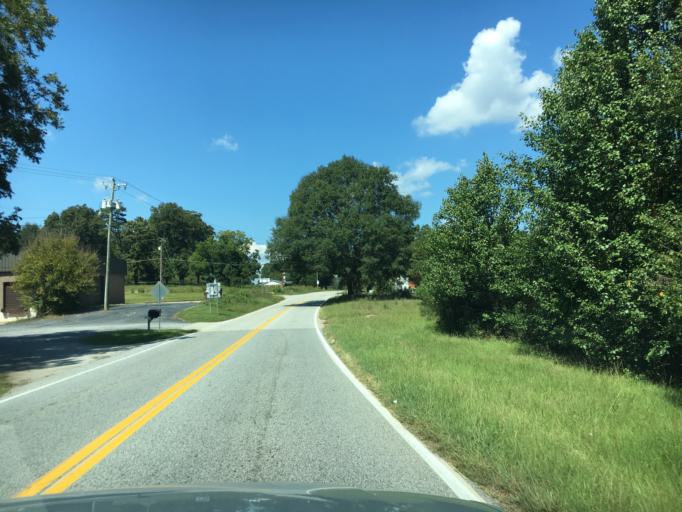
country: US
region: South Carolina
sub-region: Spartanburg County
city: Valley Falls
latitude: 35.0033
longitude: -81.9260
